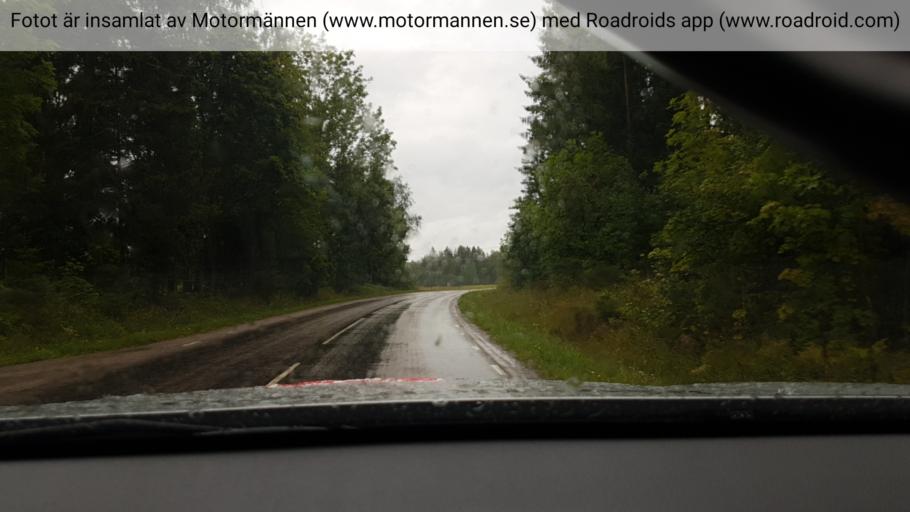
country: SE
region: Uppsala
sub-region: Tierps Kommun
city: Karlholmsbruk
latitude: 60.5131
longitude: 17.5998
